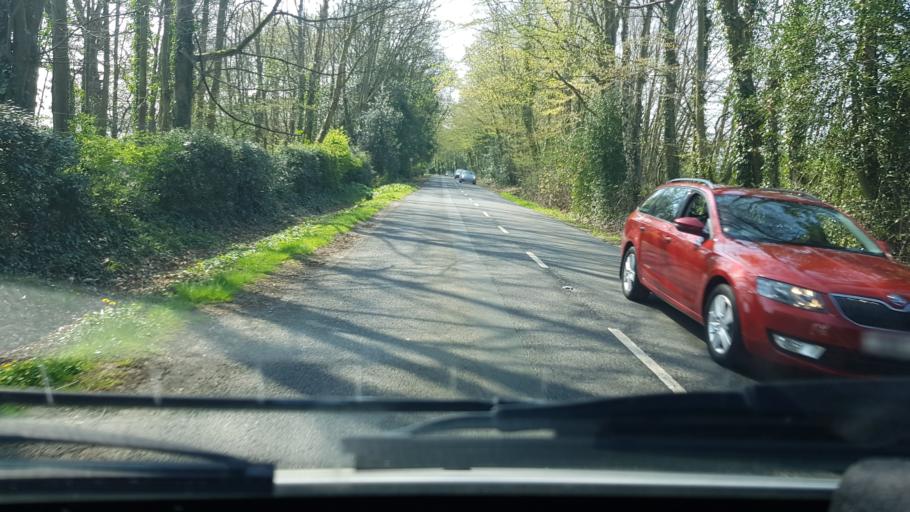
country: GB
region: England
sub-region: West Sussex
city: Chichester
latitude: 50.8524
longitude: -0.8088
